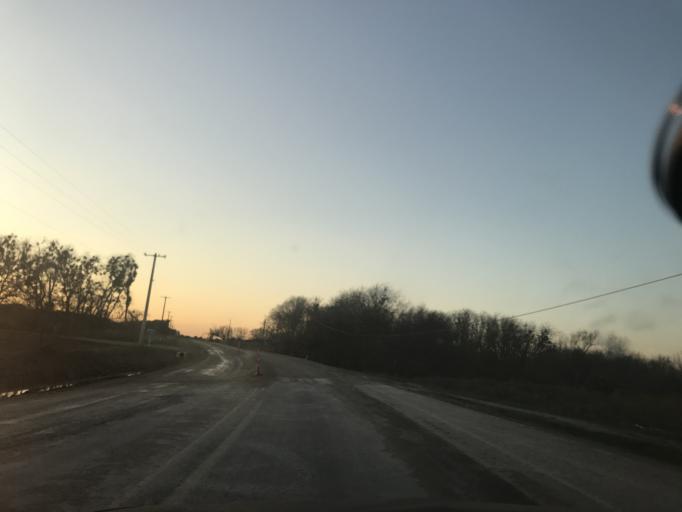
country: US
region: Texas
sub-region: Williamson County
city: Hutto
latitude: 30.5126
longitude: -97.5283
